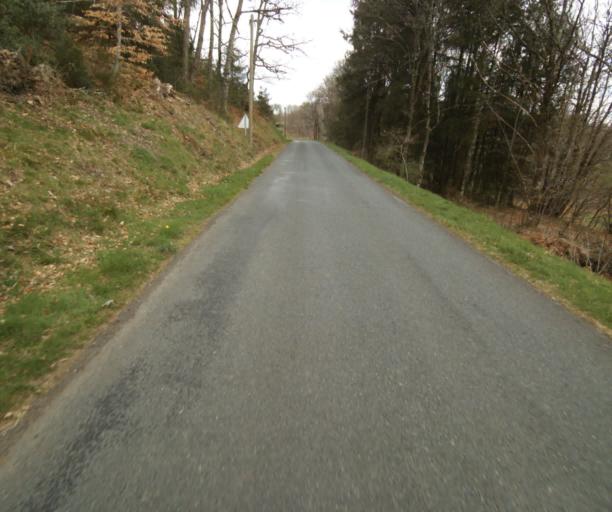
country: FR
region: Limousin
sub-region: Departement de la Correze
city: Correze
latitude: 45.3616
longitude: 1.9273
